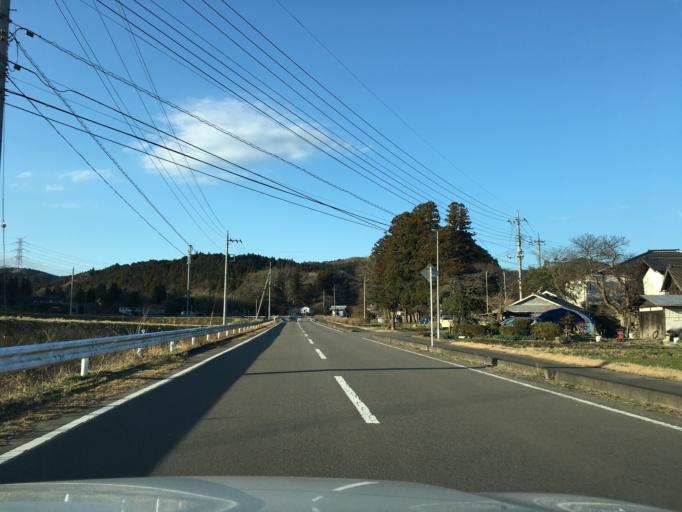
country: JP
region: Tochigi
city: Otawara
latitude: 36.8358
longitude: 140.1919
